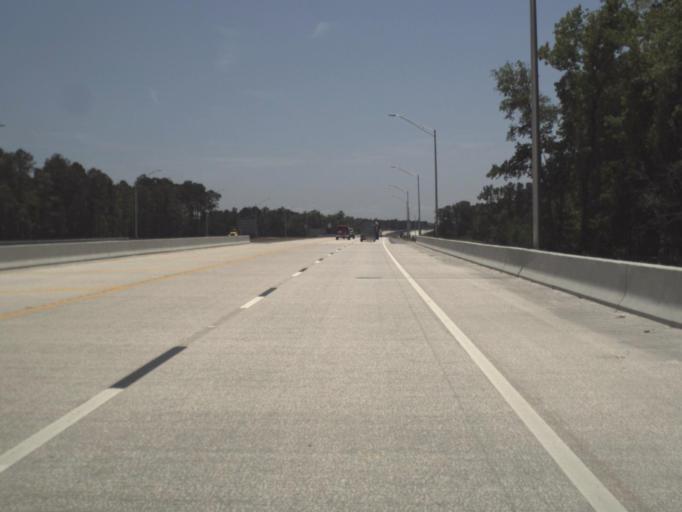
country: US
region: Florida
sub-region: Saint Johns County
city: Palm Valley
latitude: 30.1552
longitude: -81.5088
